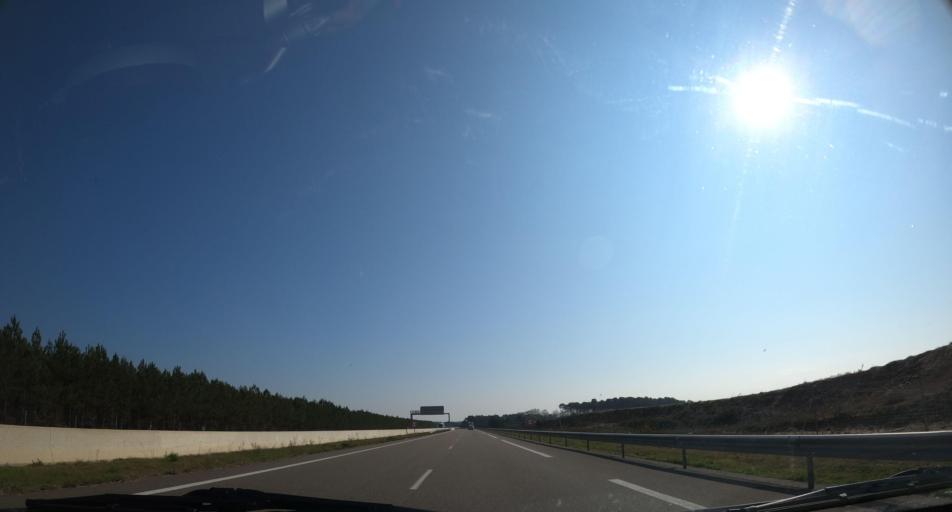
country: FR
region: Aquitaine
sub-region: Departement des Landes
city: Saint-Geours-de-Maremne
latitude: 43.6958
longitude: -1.2198
